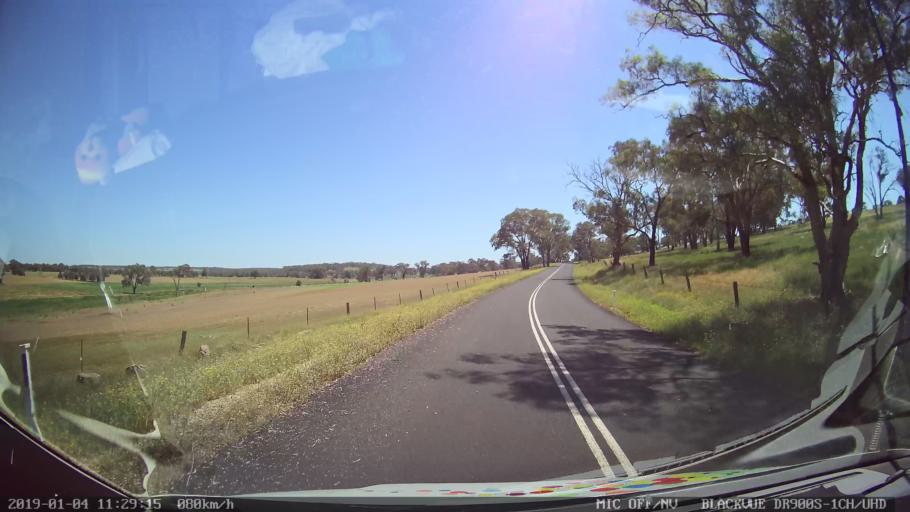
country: AU
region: New South Wales
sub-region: Cabonne
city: Molong
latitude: -33.0900
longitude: 148.7732
